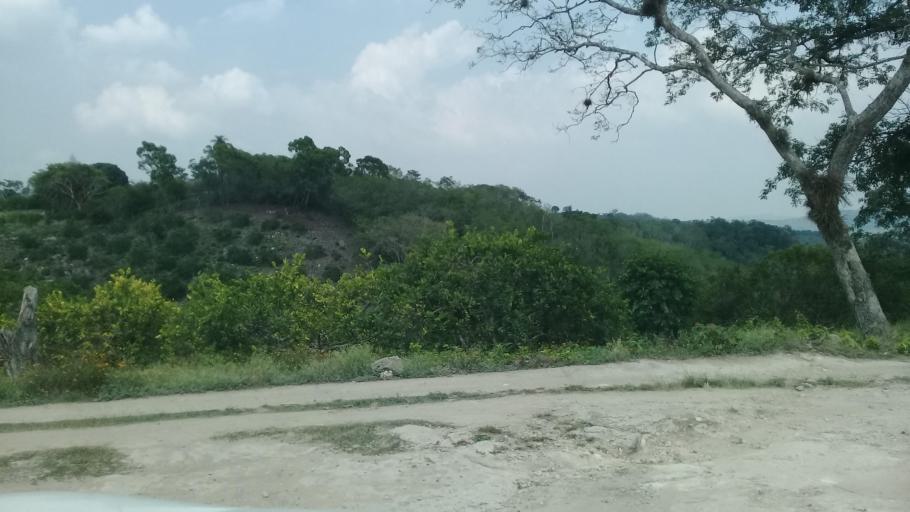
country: MX
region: Veracruz
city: Jalcomulco
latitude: 19.3891
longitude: -96.7918
